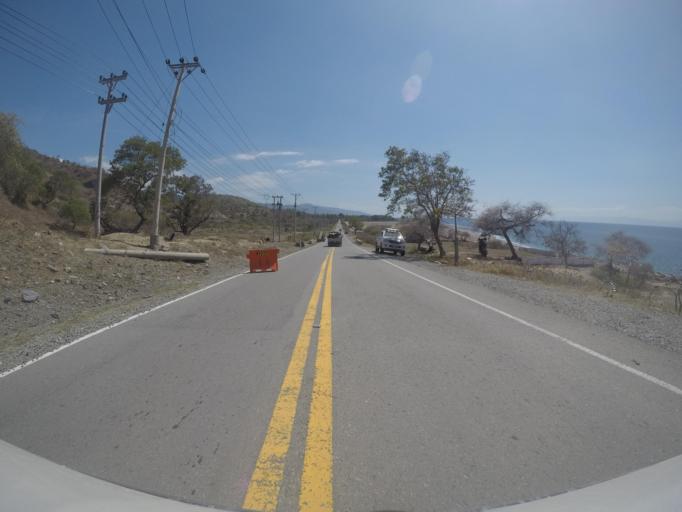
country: TL
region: Liquica
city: Liquica
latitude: -8.5768
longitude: 125.3705
